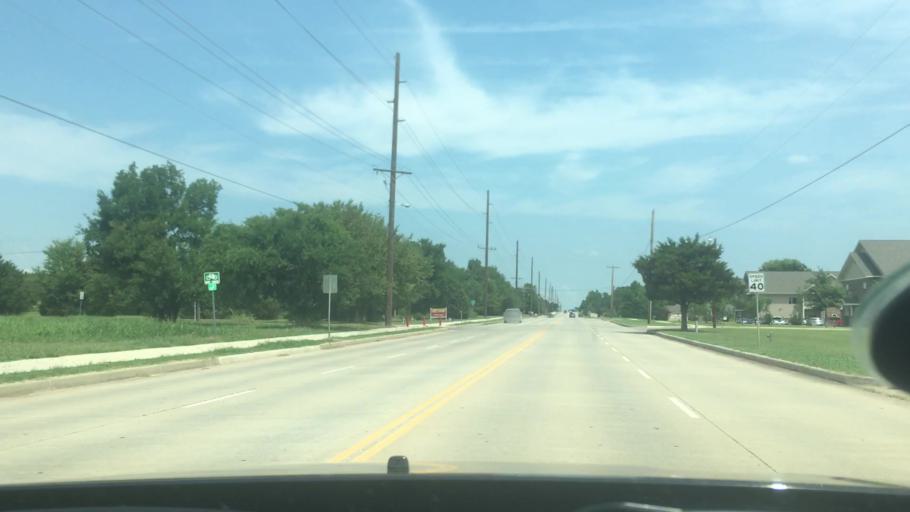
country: US
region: Oklahoma
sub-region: Pottawatomie County
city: Shawnee
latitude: 35.3519
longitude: -96.8942
